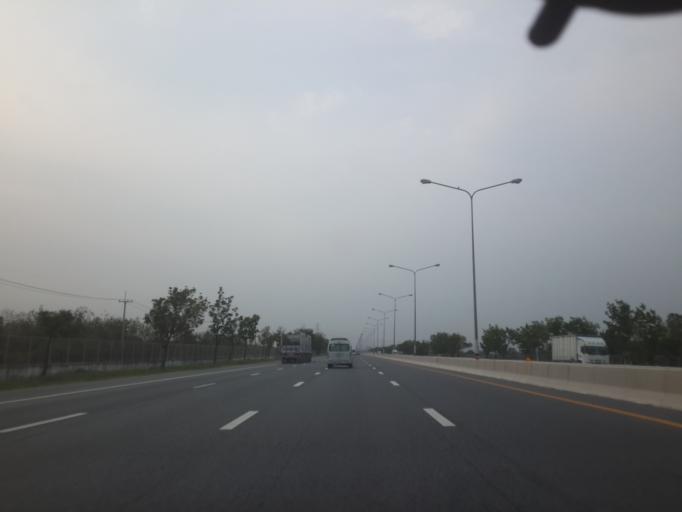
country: TH
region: Chachoengsao
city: Bang Pakong
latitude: 13.5135
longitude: 101.0305
